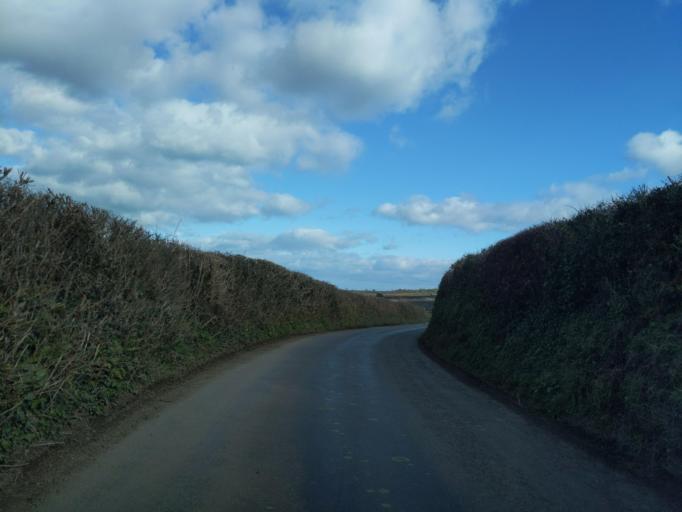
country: GB
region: England
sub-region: Devon
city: Salcombe
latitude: 50.2583
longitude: -3.7140
